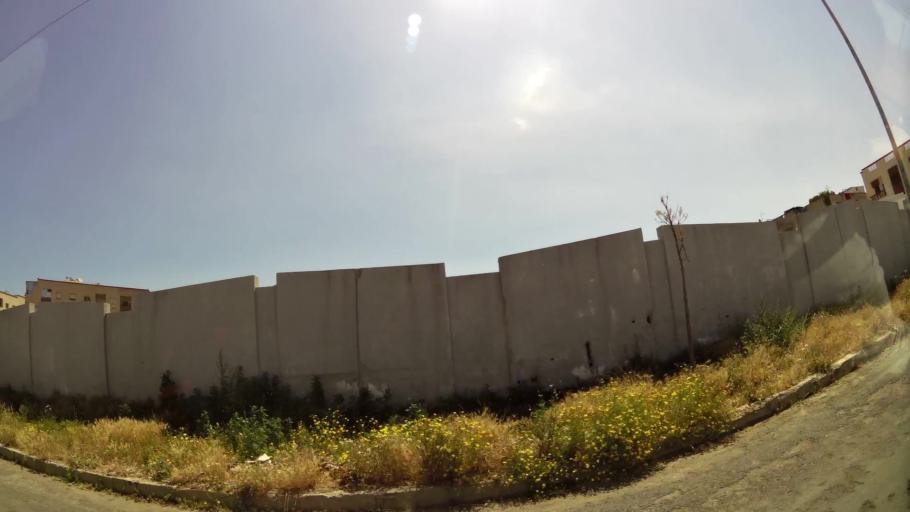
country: MA
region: Rabat-Sale-Zemmour-Zaer
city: Sale
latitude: 34.0738
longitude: -6.7896
